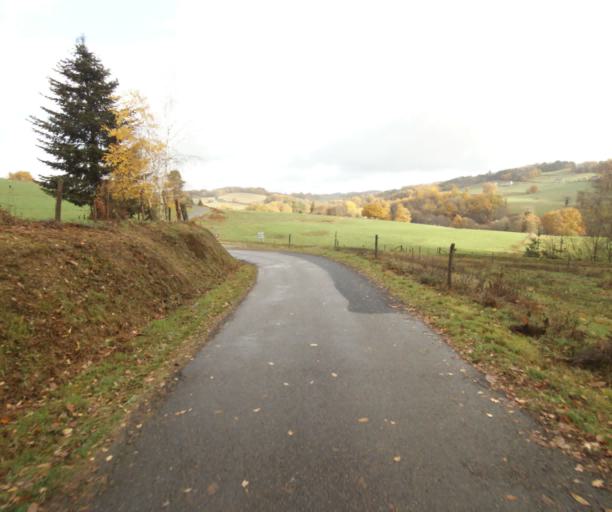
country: FR
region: Limousin
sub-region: Departement de la Correze
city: Saint-Mexant
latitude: 45.2359
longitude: 1.6378
